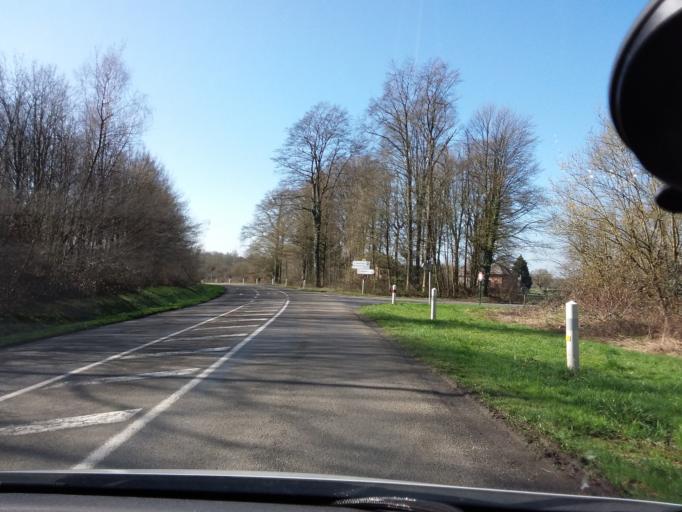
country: FR
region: Nord-Pas-de-Calais
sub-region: Departement du Nord
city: Anor
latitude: 49.9691
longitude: 4.0820
